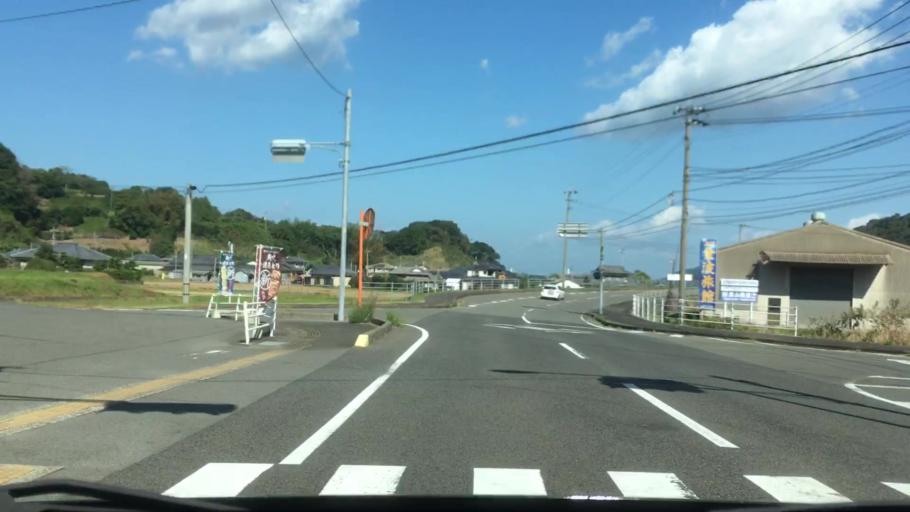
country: JP
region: Nagasaki
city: Sasebo
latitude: 32.9867
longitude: 129.6457
